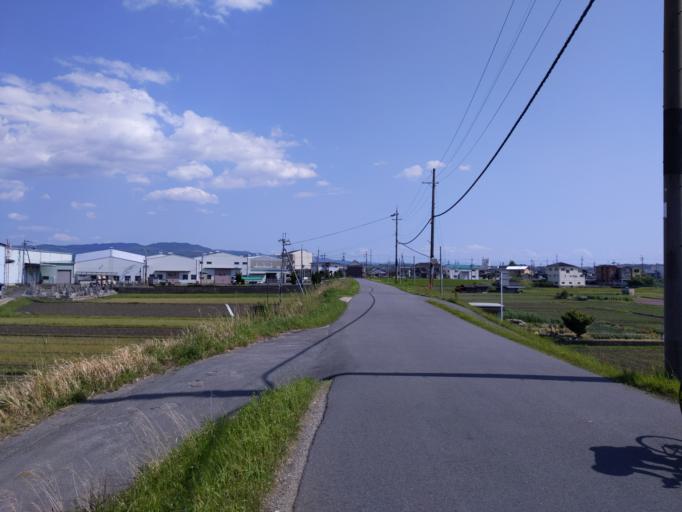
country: JP
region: Nara
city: Nara-shi
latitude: 34.7421
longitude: 135.8038
